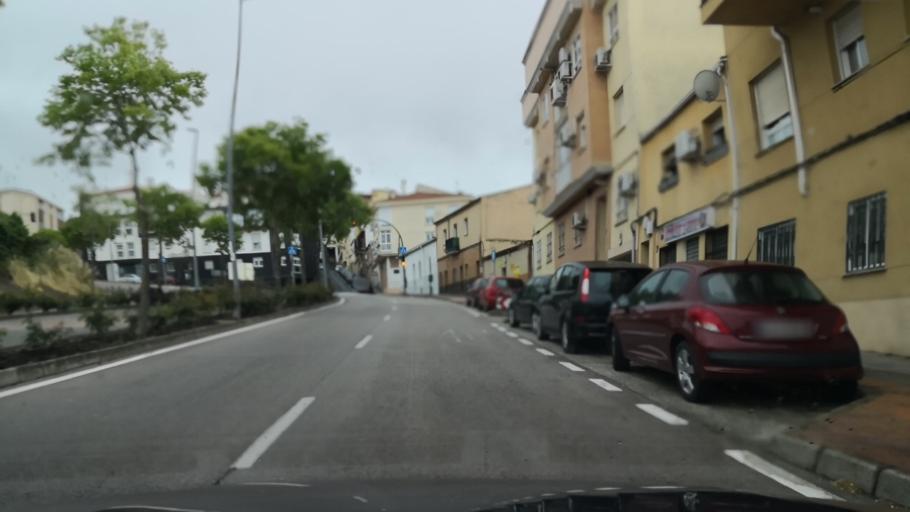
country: ES
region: Extremadura
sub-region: Provincia de Caceres
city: Caceres
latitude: 39.4806
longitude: -6.3791
